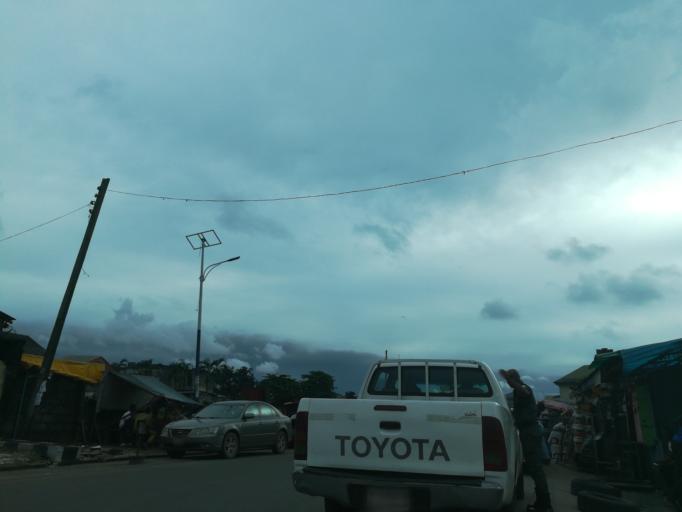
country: NG
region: Rivers
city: Port Harcourt
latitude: 4.8084
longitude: 6.9920
